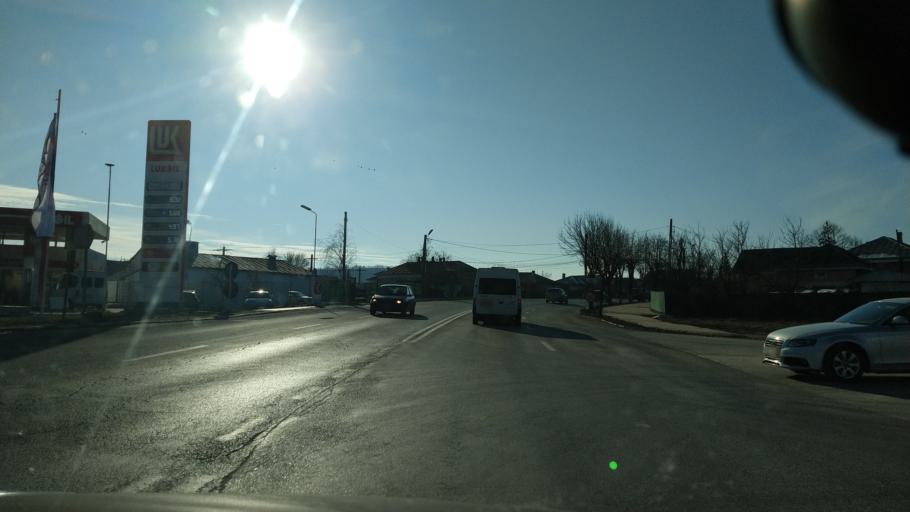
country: RO
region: Iasi
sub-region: Comuna Ion Neculce
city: Buznea
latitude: 47.2119
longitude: 27.0243
